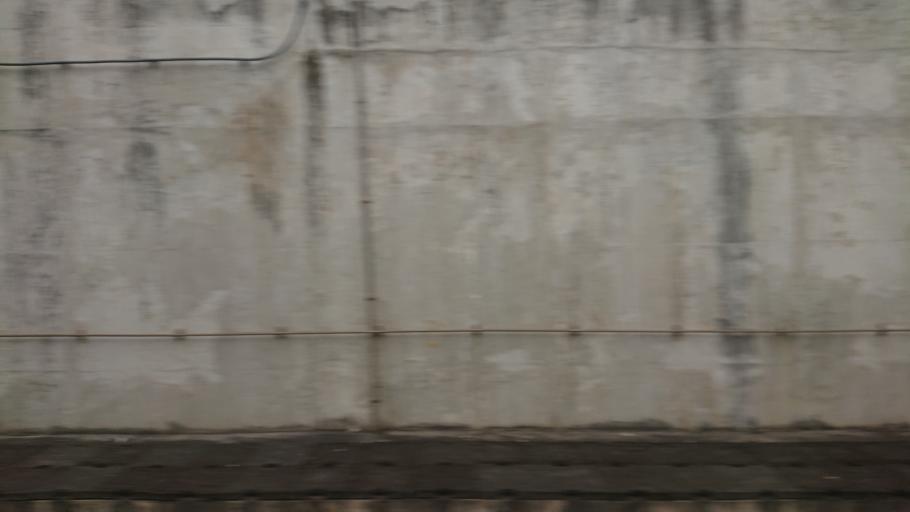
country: TW
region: Taiwan
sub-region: Hualien
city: Hualian
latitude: 23.8217
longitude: 121.4772
